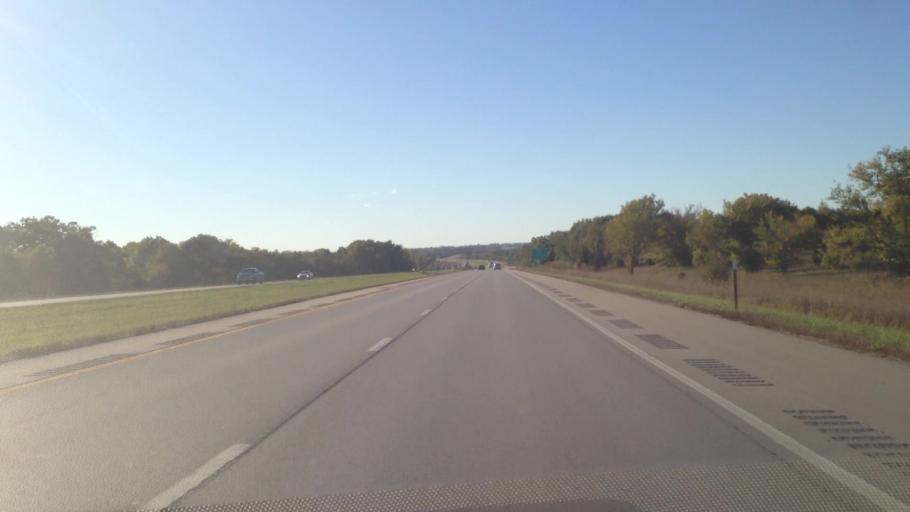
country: US
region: Kansas
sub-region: Douglas County
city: Eudora
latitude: 38.9331
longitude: -95.1259
